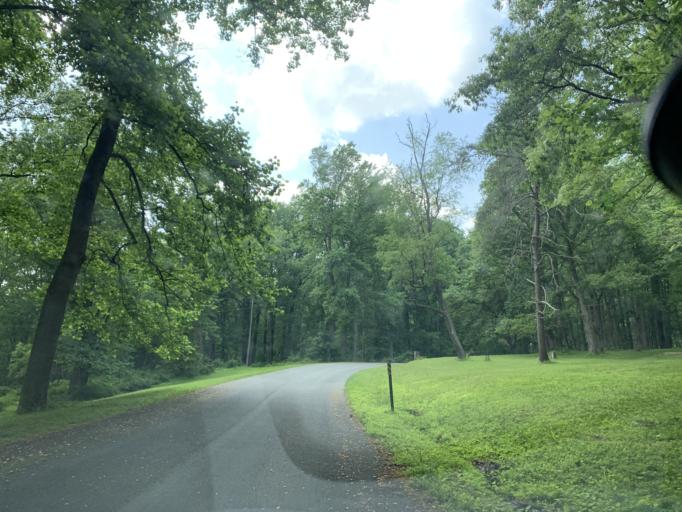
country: US
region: Maryland
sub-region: Carroll County
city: Eldersburg
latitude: 39.3568
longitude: -76.8842
